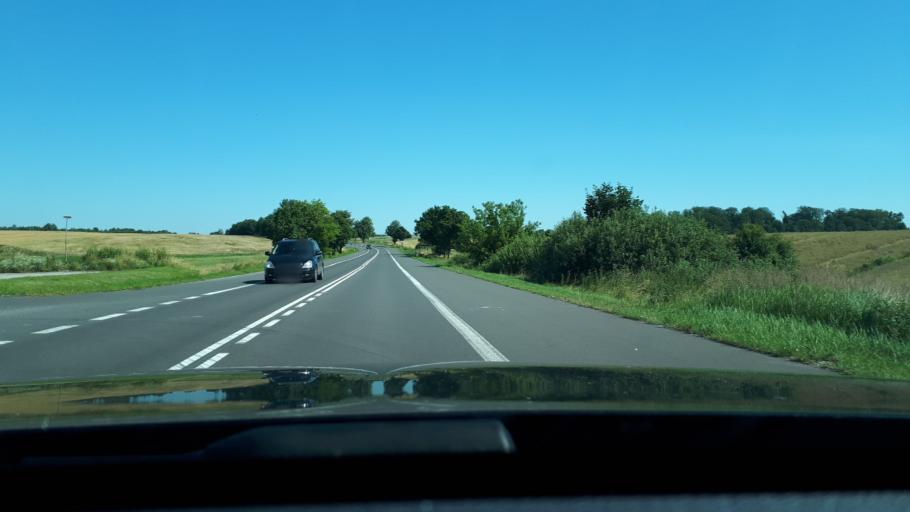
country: PL
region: Warmian-Masurian Voivodeship
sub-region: Powiat ostrodzki
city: Ostroda
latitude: 53.6513
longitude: 20.0515
